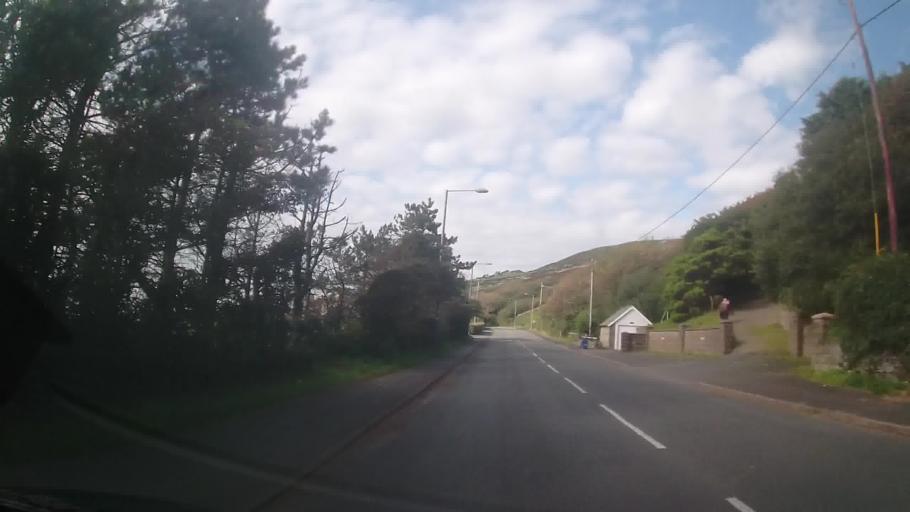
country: GB
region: Wales
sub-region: Gwynedd
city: Barmouth
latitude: 52.7332
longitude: -4.0660
